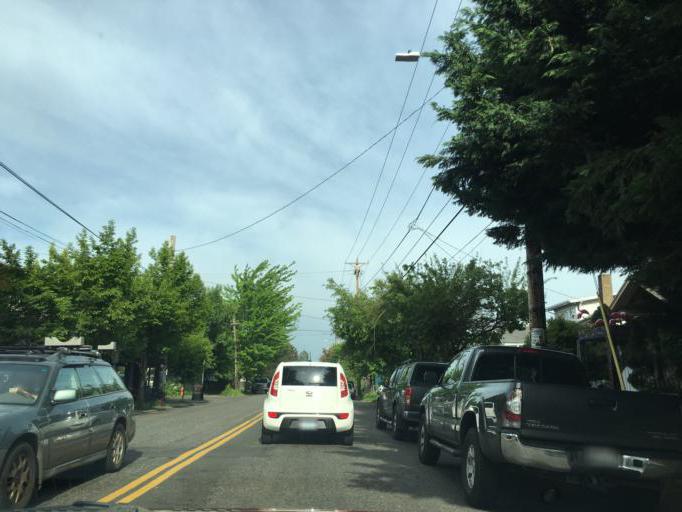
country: US
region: Oregon
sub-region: Multnomah County
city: Lents
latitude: 45.5052
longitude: -122.6159
